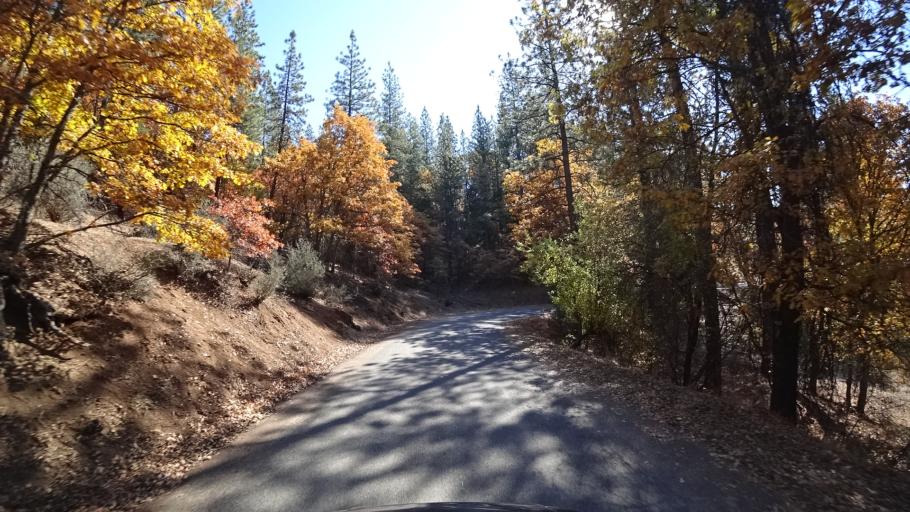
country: US
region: California
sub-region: Siskiyou County
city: Yreka
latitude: 41.6080
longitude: -122.9620
